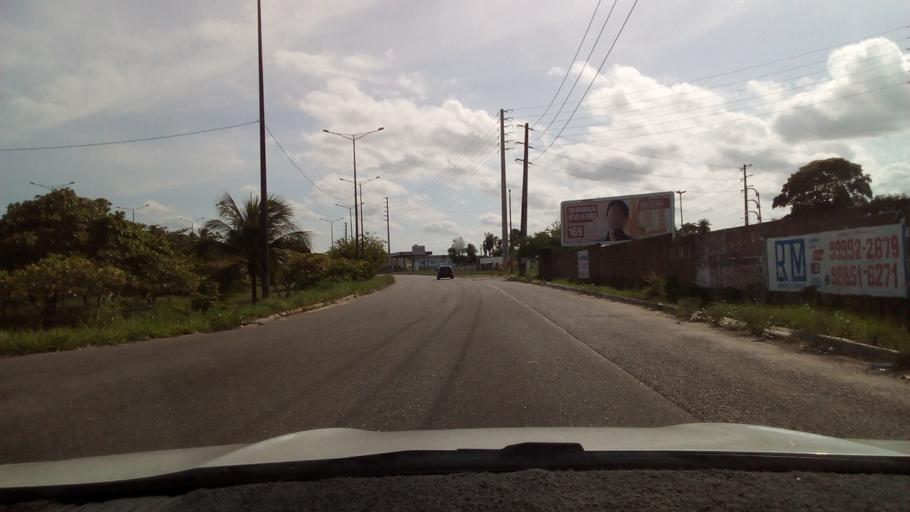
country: BR
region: Paraiba
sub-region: Bayeux
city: Bayeux
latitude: -7.1447
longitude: -34.9072
